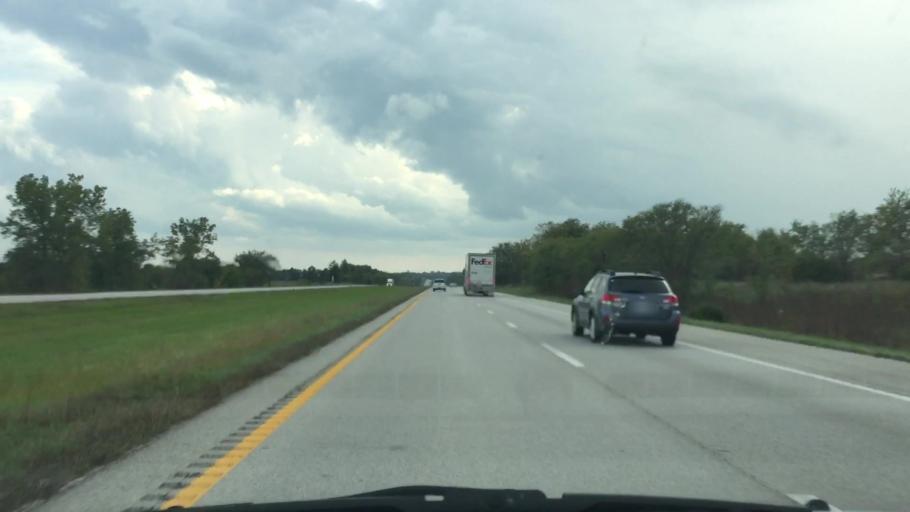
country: US
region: Missouri
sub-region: Clinton County
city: Cameron
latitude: 39.7833
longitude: -94.2081
